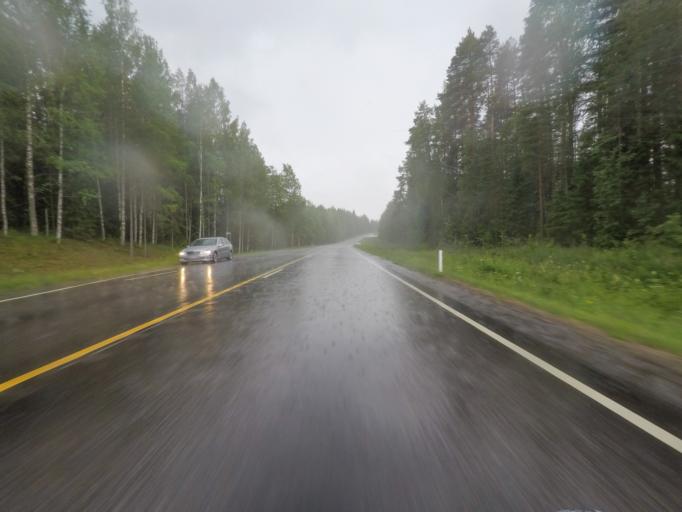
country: FI
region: Central Finland
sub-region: Jyvaeskylae
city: Hankasalmi
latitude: 62.3717
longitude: 26.5847
